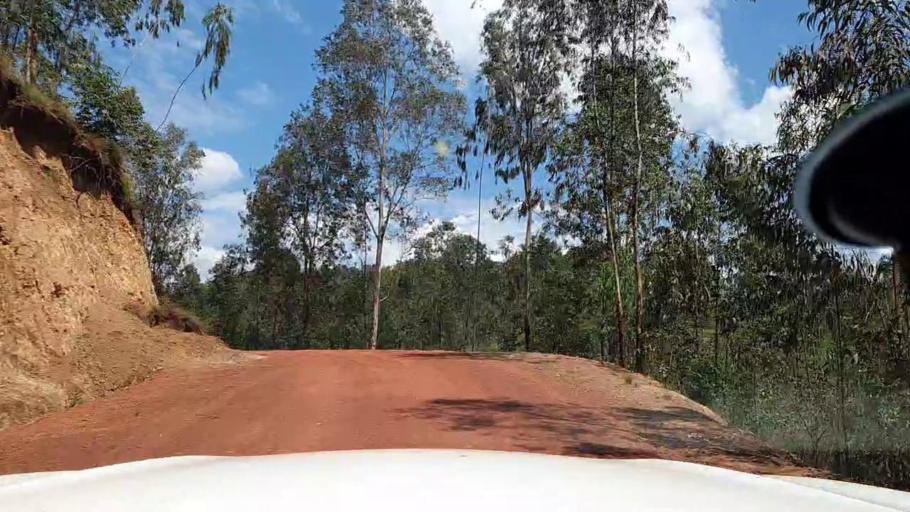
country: RW
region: Kigali
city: Kigali
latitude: -1.7662
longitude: 29.8741
